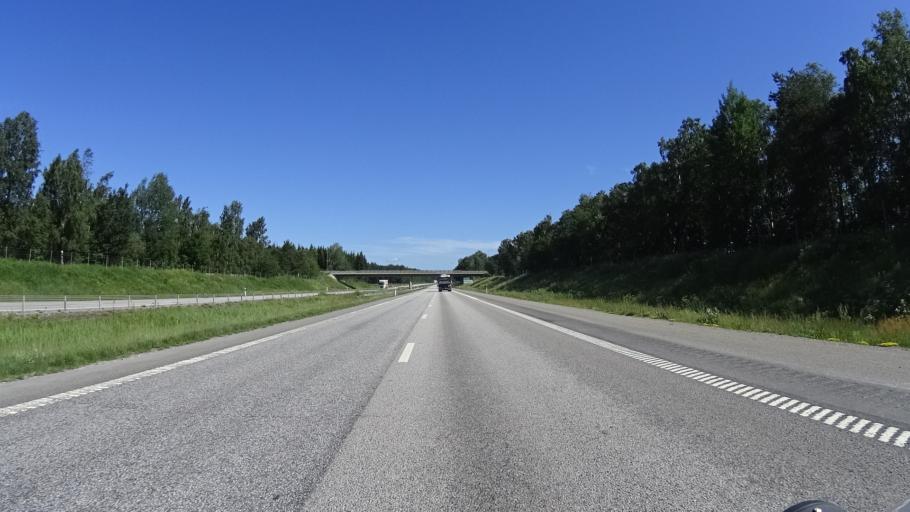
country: SE
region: OErebro
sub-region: Hallsbergs Kommun
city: Hallsberg
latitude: 59.1219
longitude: 15.0720
